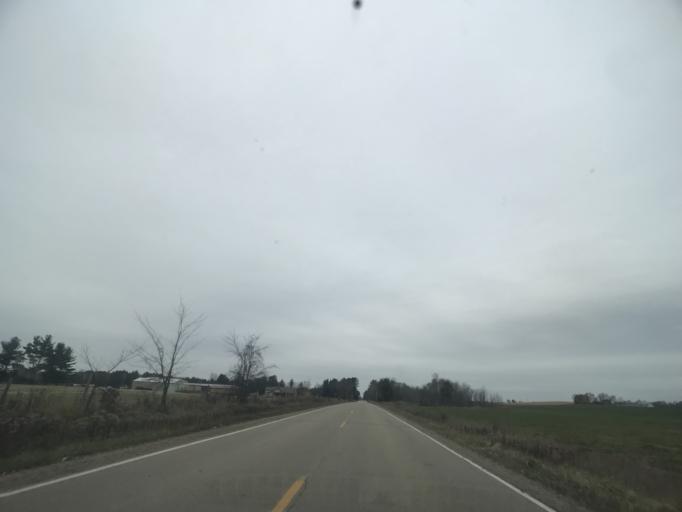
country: US
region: Wisconsin
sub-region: Oconto County
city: Gillett
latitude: 44.9837
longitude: -88.3169
